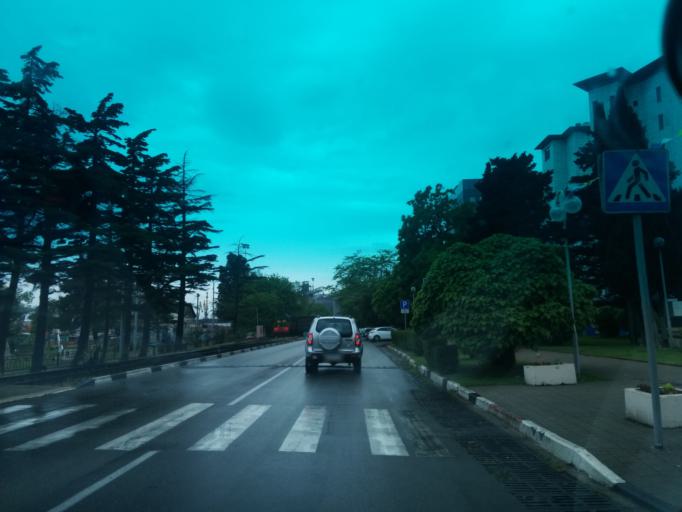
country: RU
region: Krasnodarskiy
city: Tuapse
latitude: 44.0946
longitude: 39.0730
